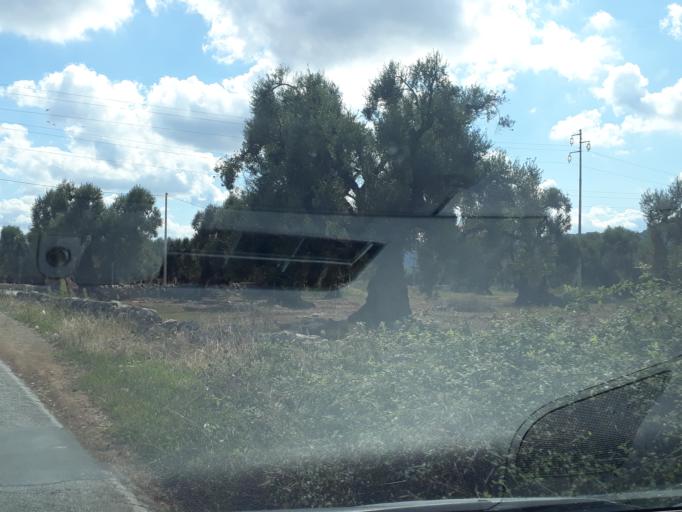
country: IT
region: Apulia
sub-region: Provincia di Brindisi
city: Fasano
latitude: 40.8265
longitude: 17.3694
